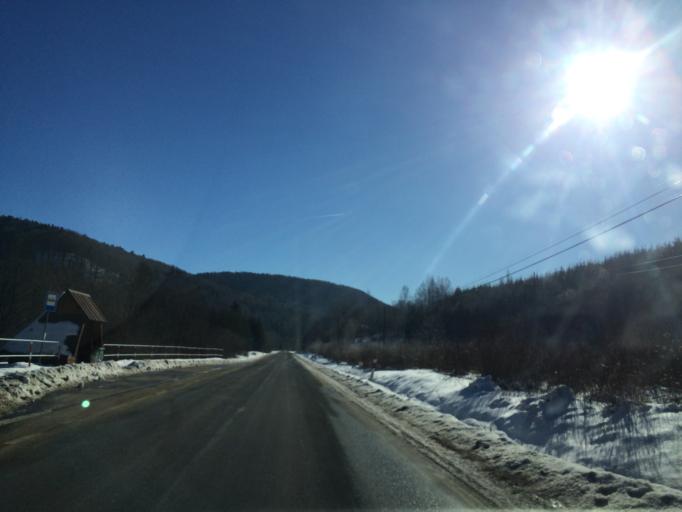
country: PL
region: Subcarpathian Voivodeship
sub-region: Powiat bieszczadzki
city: Lutowiska
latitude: 49.1980
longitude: 22.6767
